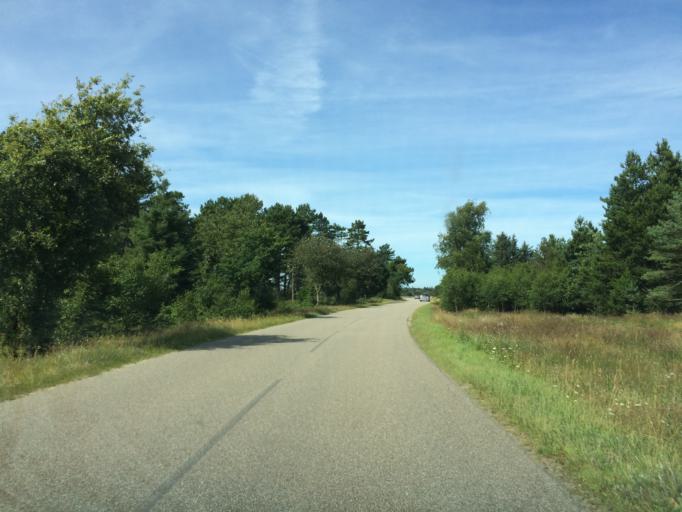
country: DK
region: South Denmark
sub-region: Varde Kommune
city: Oksbol
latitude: 55.6725
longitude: 8.1894
